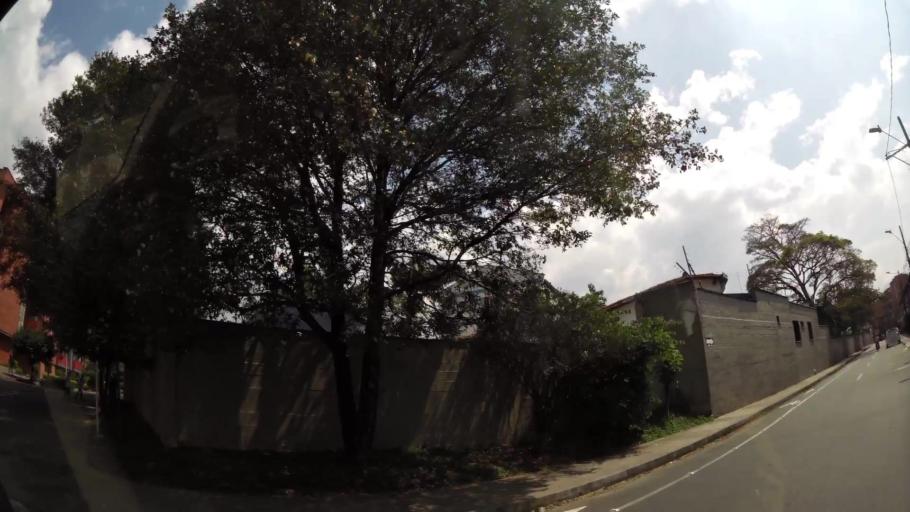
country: CO
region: Antioquia
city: Envigado
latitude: 6.1700
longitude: -75.5929
